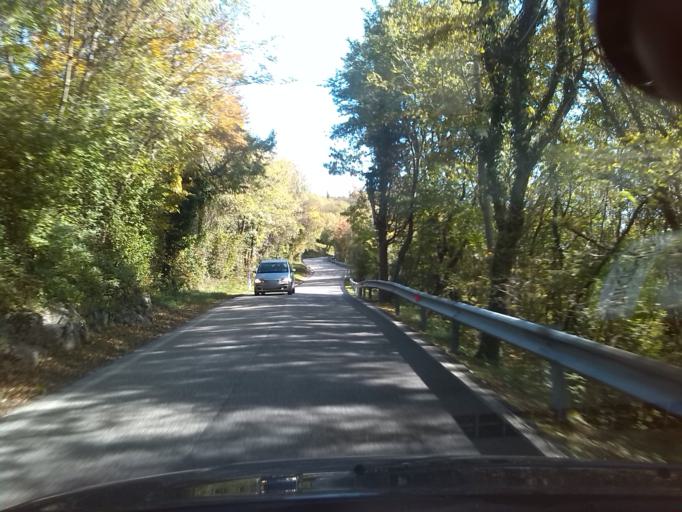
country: IT
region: Friuli Venezia Giulia
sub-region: Provincia di Udine
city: San Pietro al Natisone
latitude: 46.0899
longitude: 13.4914
